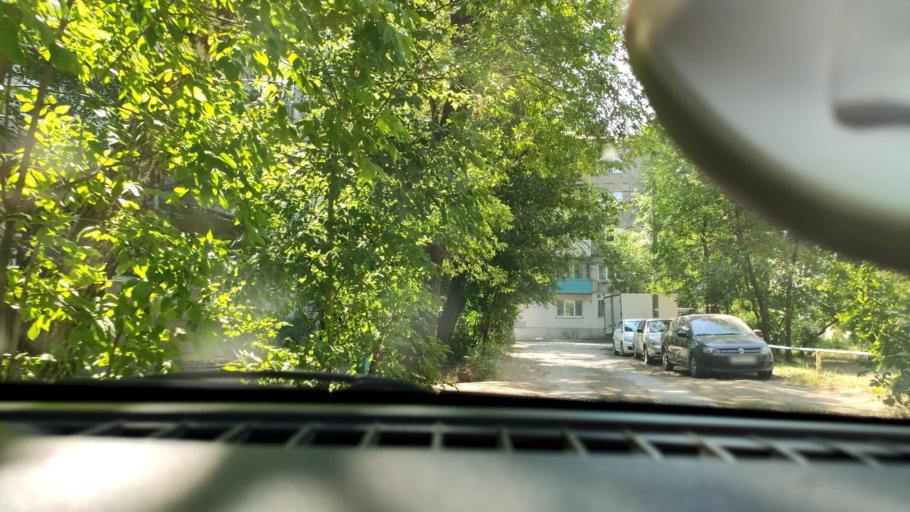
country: RU
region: Samara
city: Samara
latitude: 53.1244
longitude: 50.0914
